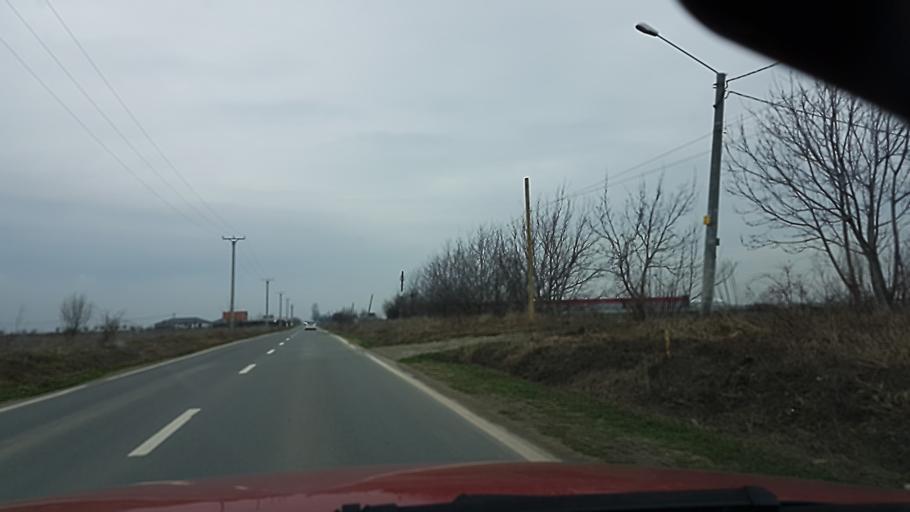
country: RO
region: Ilfov
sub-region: Comuna Balotesti
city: Balotesti
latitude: 44.6176
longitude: 26.1256
